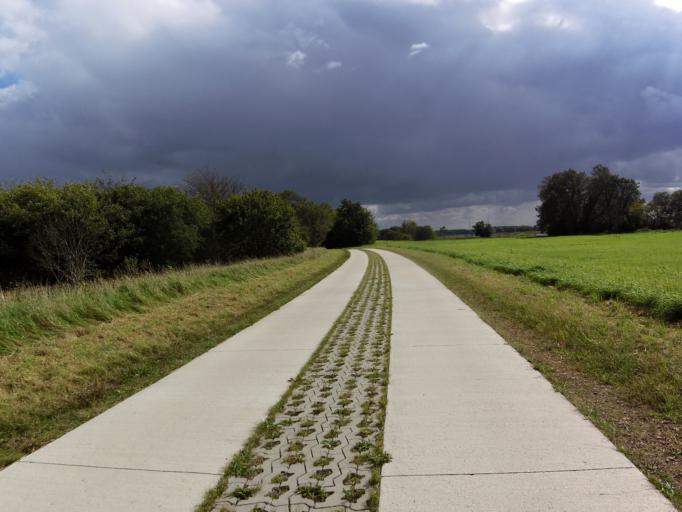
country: DE
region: Saxony-Anhalt
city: Barby
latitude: 51.9716
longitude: 11.8982
